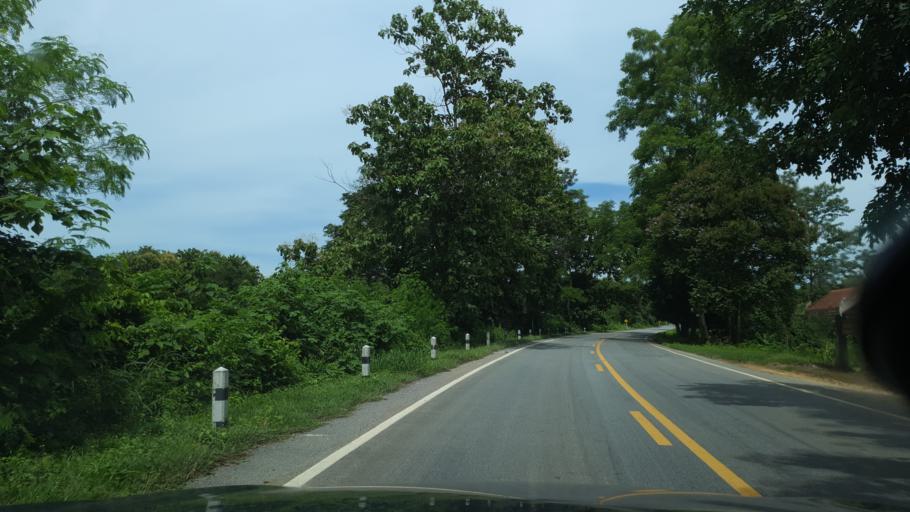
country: TH
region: Sukhothai
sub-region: Amphoe Si Satchanalai
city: Si Satchanalai
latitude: 17.6180
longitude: 99.7075
